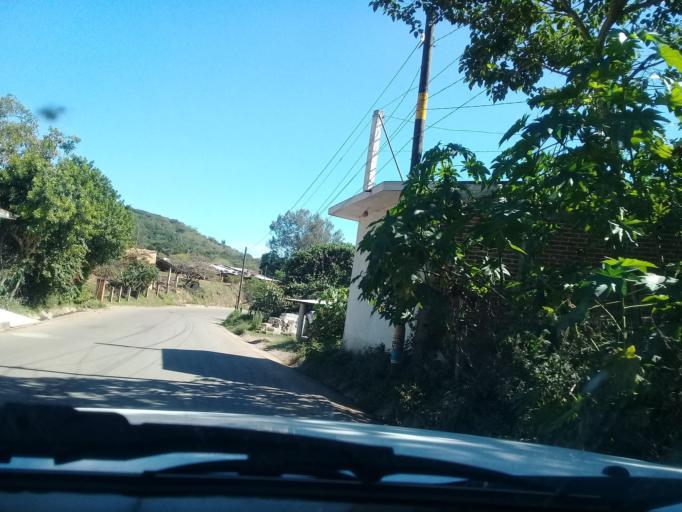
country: MX
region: Veracruz
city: El Castillo
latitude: 19.5490
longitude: -96.8514
